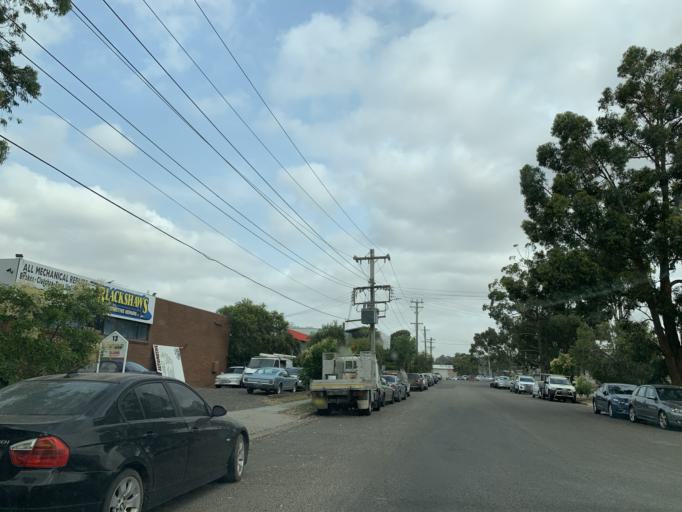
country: AU
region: New South Wales
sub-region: Parramatta
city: Constitution Hill
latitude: -33.7736
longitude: 150.9572
